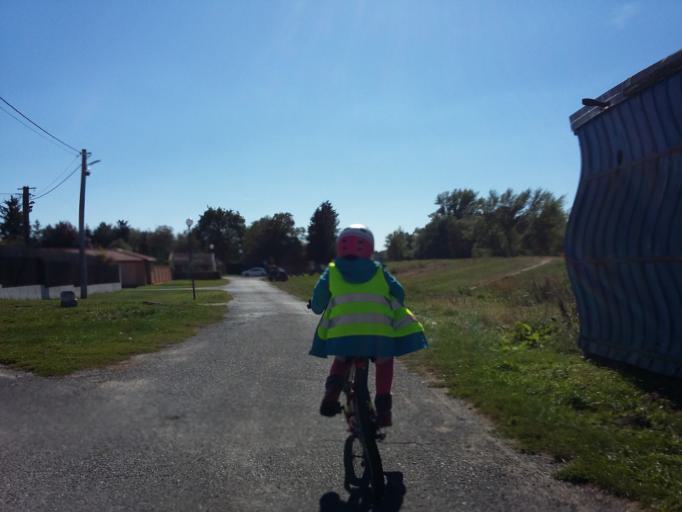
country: AT
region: Lower Austria
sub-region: Politischer Bezirk Ganserndorf
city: Marchegg
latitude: 48.3235
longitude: 16.9100
